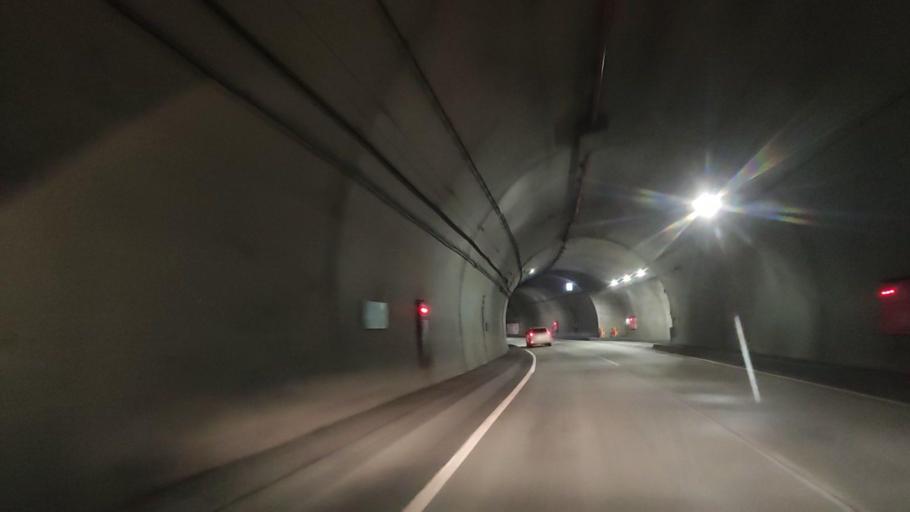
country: JP
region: Hokkaido
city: Rumoi
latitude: 43.7125
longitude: 141.3312
